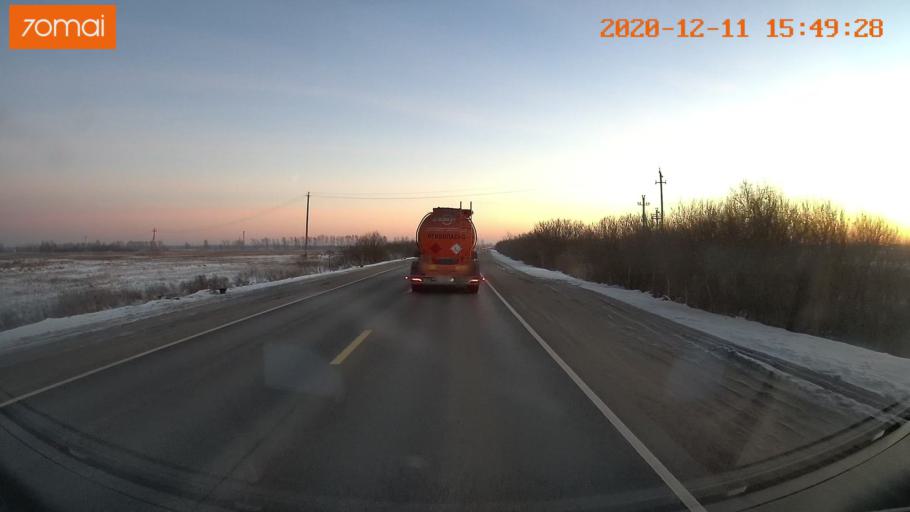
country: RU
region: Ivanovo
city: Novo-Talitsy
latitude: 56.9879
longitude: 40.8746
